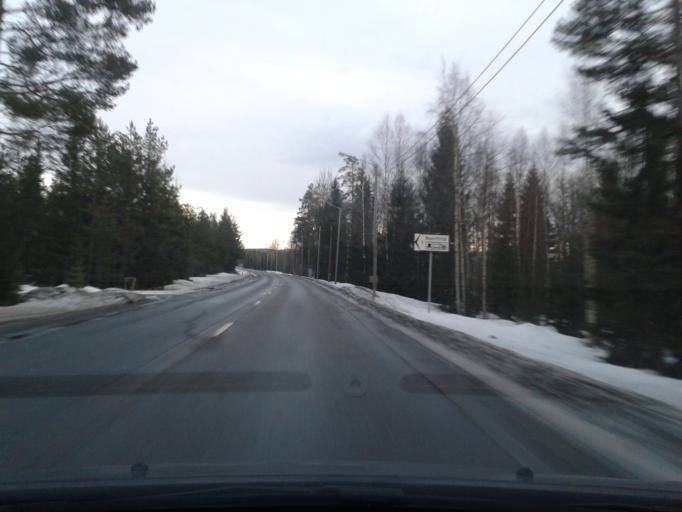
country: SE
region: Vaesternorrland
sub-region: Solleftea Kommun
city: Solleftea
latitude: 63.1528
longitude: 17.3320
